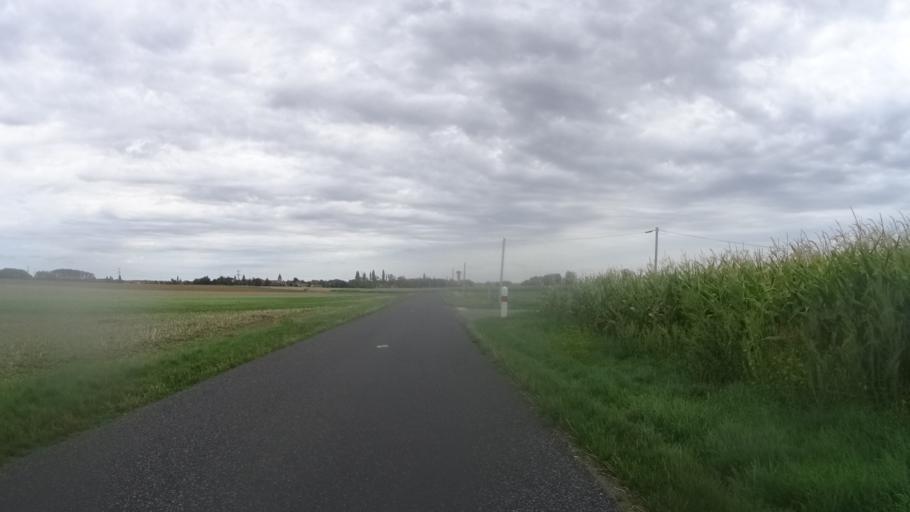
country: FR
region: Centre
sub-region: Departement du Loiret
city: Boynes
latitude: 48.0885
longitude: 2.3075
